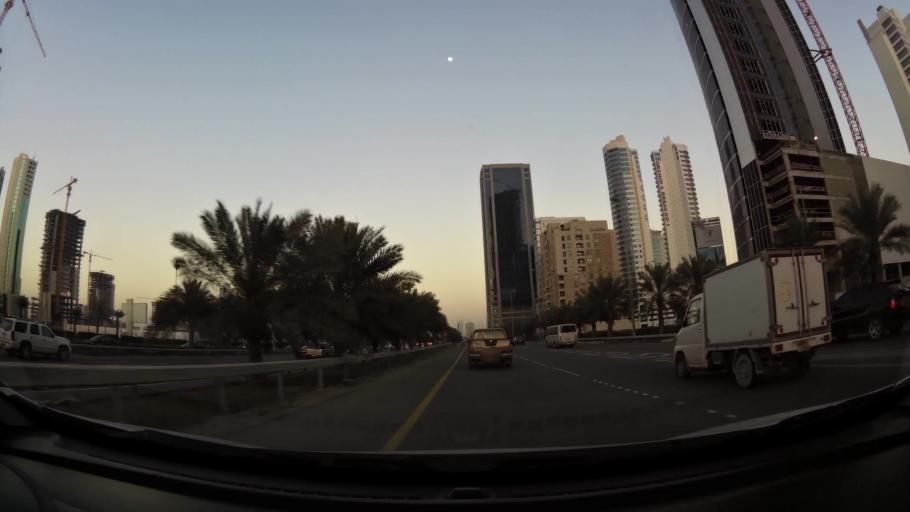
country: BH
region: Manama
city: Jidd Hafs
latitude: 26.2314
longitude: 50.5473
